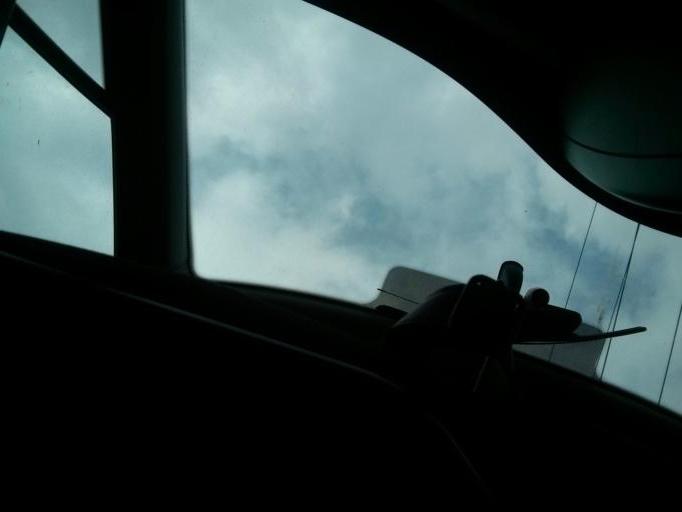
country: RU
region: Perm
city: Kondratovo
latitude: 57.9963
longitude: 56.1358
